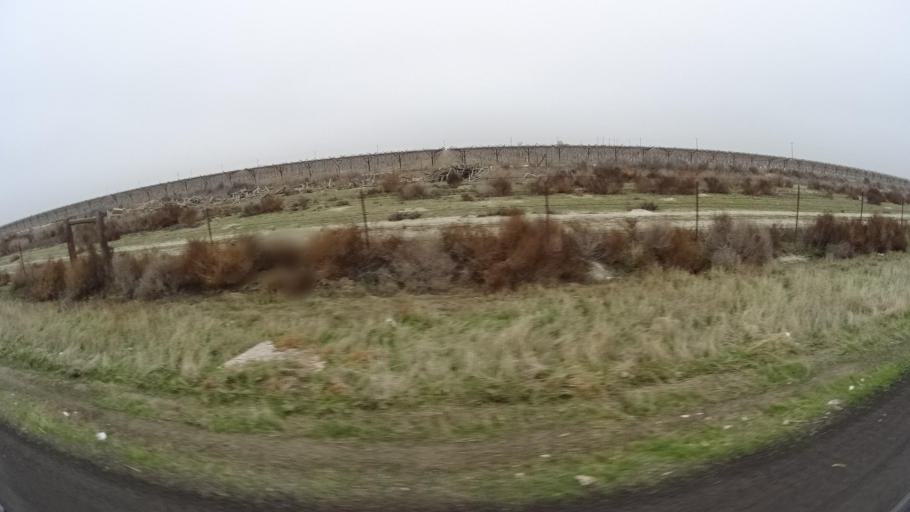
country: US
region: California
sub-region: Tulare County
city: Alpaugh
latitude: 35.7627
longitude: -119.4775
